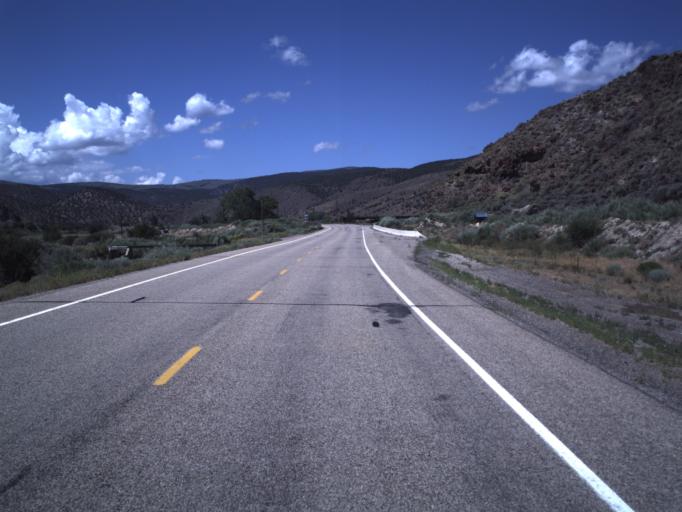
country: US
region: Utah
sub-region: Piute County
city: Junction
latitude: 38.1518
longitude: -112.2892
